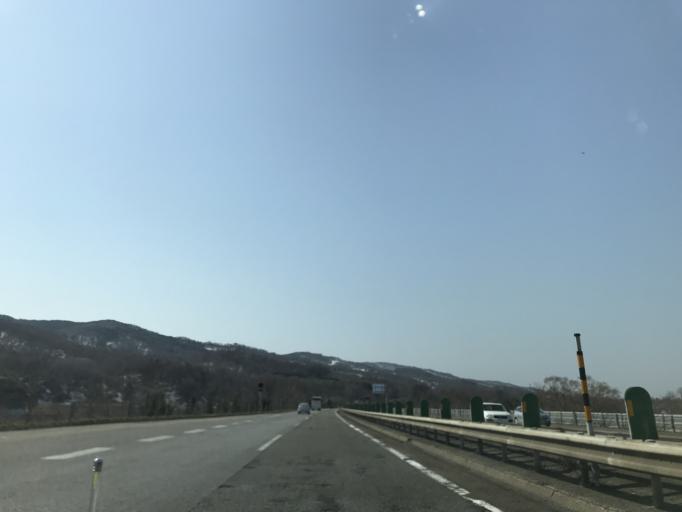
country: JP
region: Hokkaido
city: Bibai
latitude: 43.3305
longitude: 141.8882
